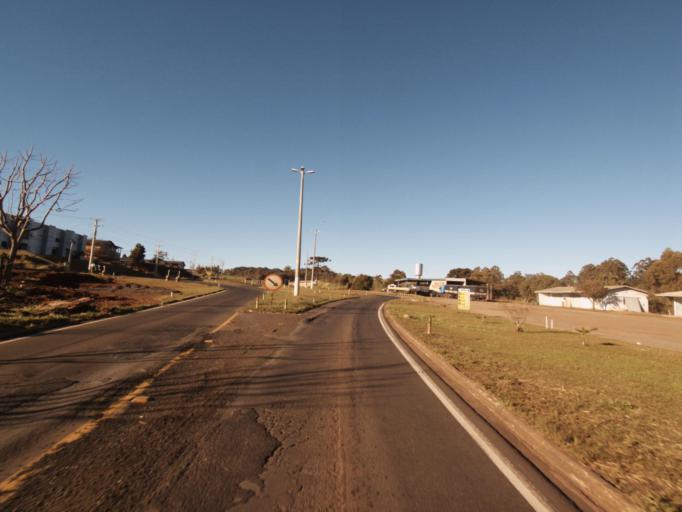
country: AR
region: Misiones
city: Bernardo de Irigoyen
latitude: -26.4332
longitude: -53.5191
